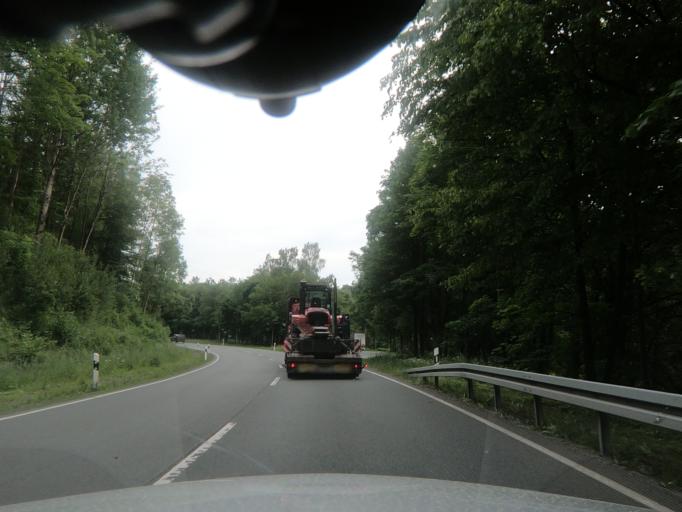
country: DE
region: North Rhine-Westphalia
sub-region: Regierungsbezirk Arnsberg
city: Winterberg
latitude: 51.2704
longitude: 8.5203
